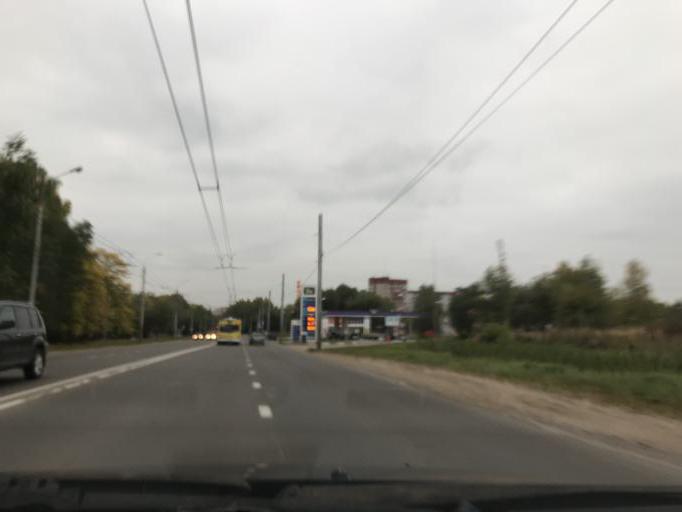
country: RU
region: Kaluga
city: Kaluga
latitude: 54.5959
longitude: 36.2592
